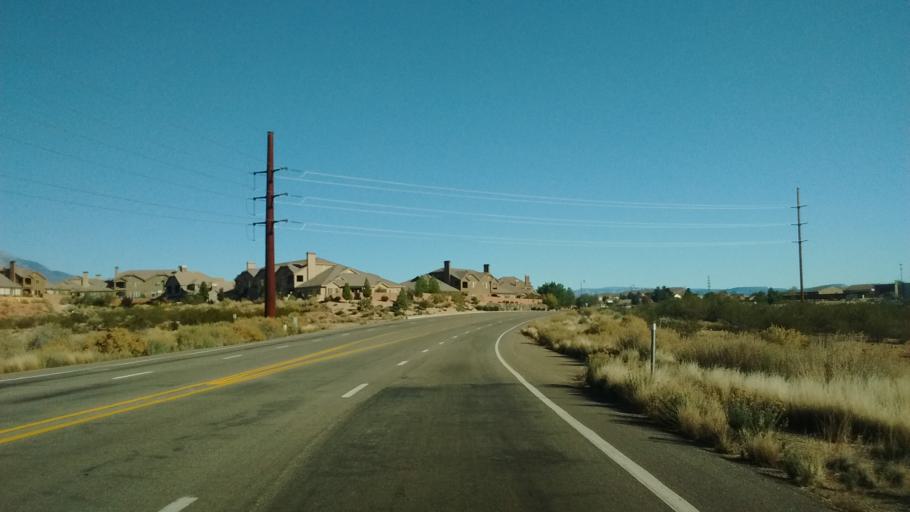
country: US
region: Utah
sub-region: Washington County
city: Washington
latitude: 37.1548
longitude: -113.4424
